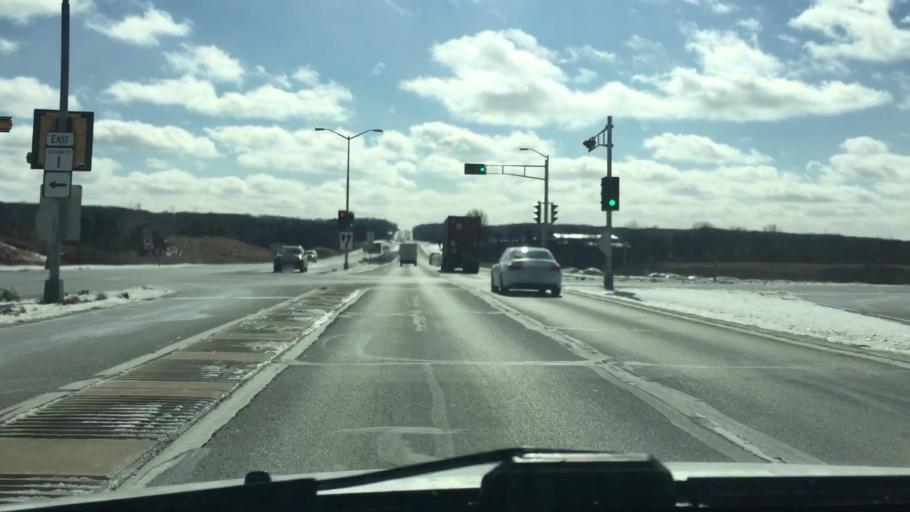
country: US
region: Wisconsin
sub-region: Waukesha County
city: Waukesha
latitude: 42.9596
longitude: -88.2281
